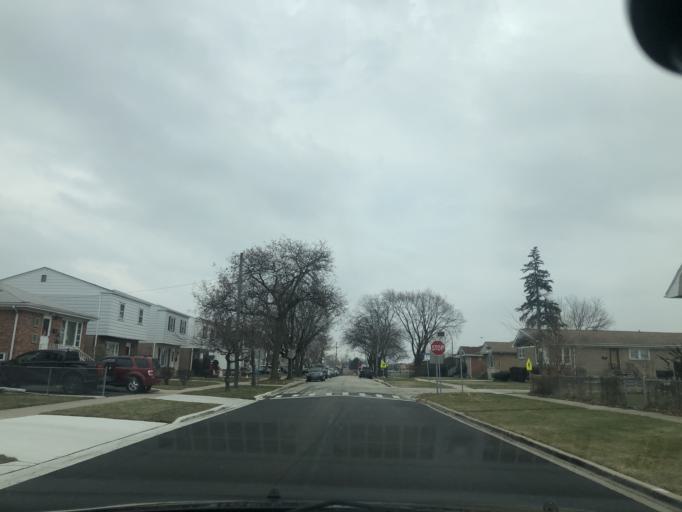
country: US
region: Illinois
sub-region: Cook County
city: Schiller Park
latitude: 41.9684
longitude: -87.8674
